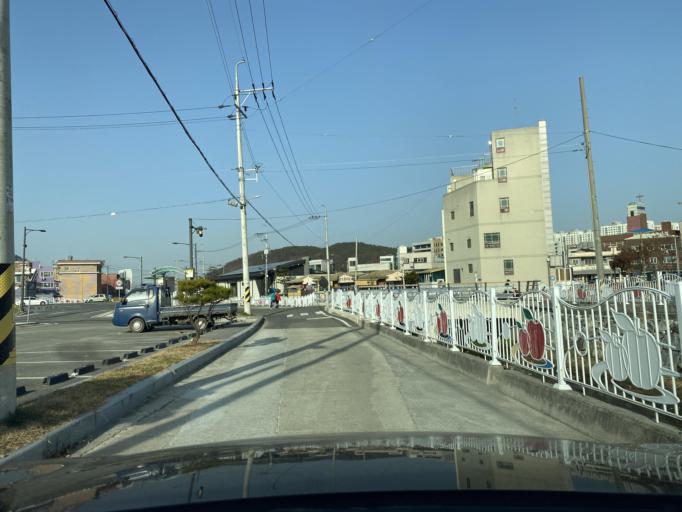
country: KR
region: Chungcheongnam-do
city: Yesan
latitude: 36.6756
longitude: 126.8491
